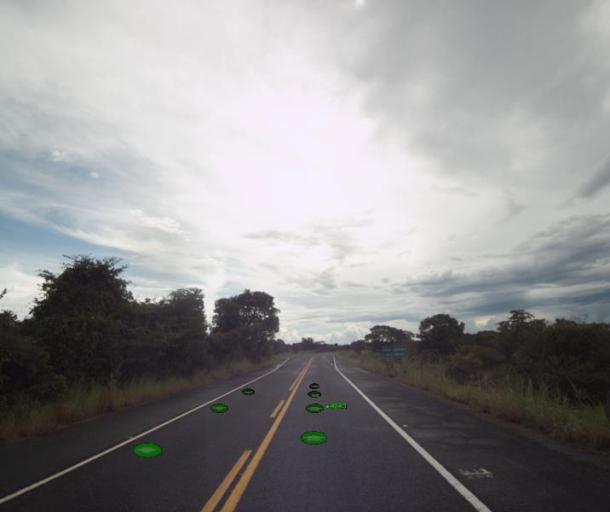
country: BR
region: Goias
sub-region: Sao Miguel Do Araguaia
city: Sao Miguel do Araguaia
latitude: -13.2344
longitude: -50.5608
